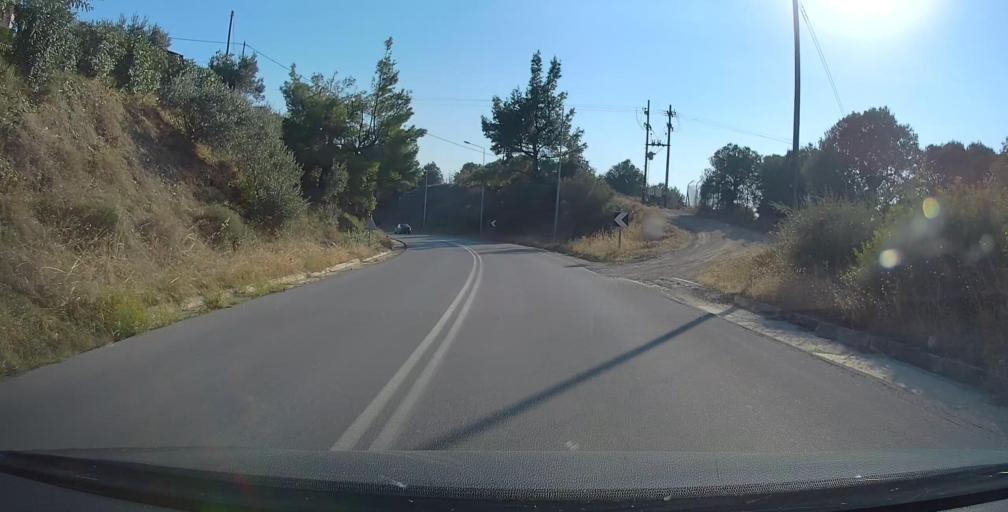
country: GR
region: Central Macedonia
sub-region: Nomos Chalkidikis
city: Neos Marmaras
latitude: 40.0813
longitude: 23.8061
